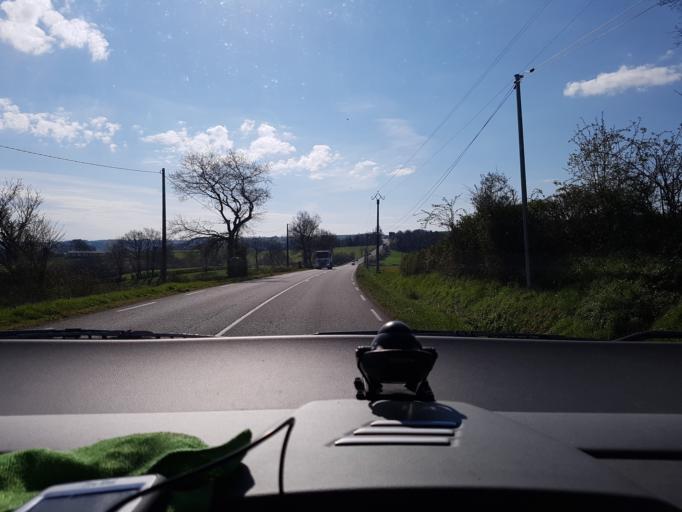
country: FR
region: Midi-Pyrenees
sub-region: Departement de l'Aveyron
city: Moyrazes
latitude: 44.3902
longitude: 2.3956
